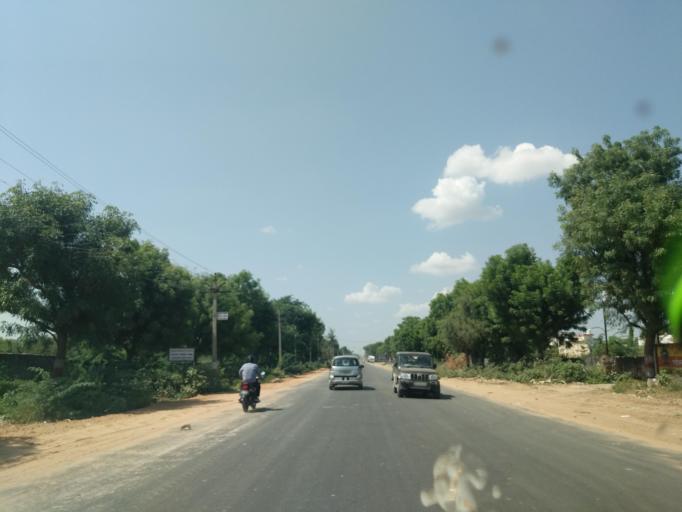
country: IN
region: Rajasthan
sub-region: Nagaur
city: Makrana
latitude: 27.0250
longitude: 74.7594
